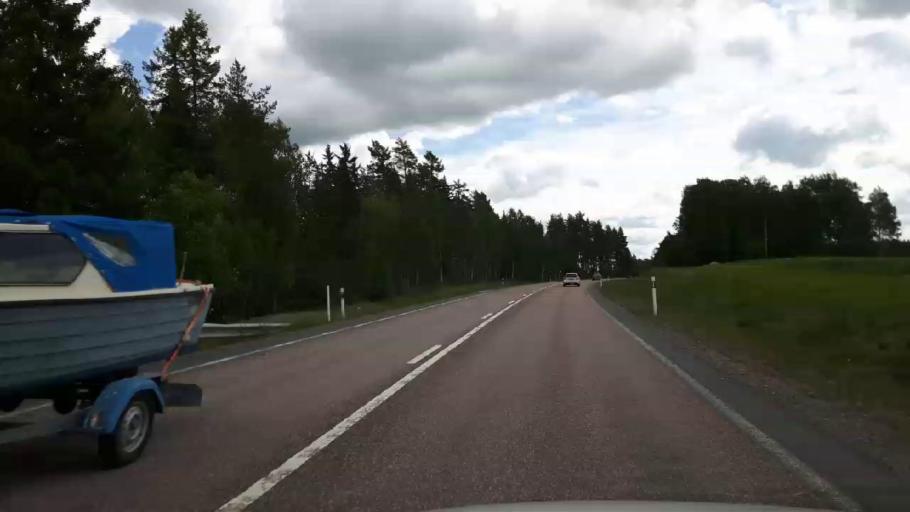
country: SE
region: Dalarna
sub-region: Saters Kommun
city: Saeter
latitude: 60.4713
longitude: 15.7949
